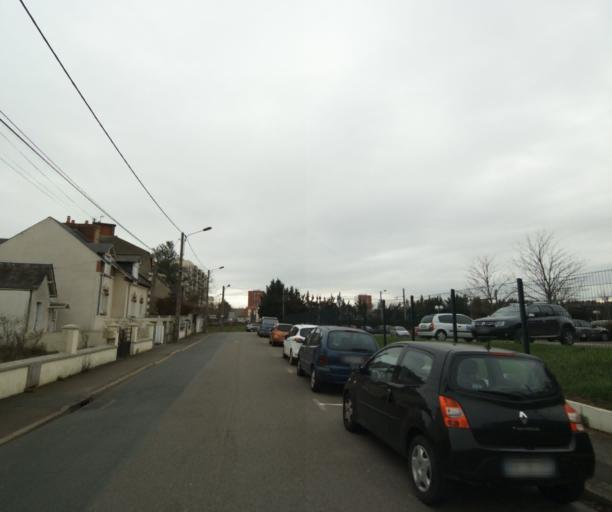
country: FR
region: Pays de la Loire
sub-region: Departement de la Sarthe
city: Le Mans
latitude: 47.9952
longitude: 0.2209
